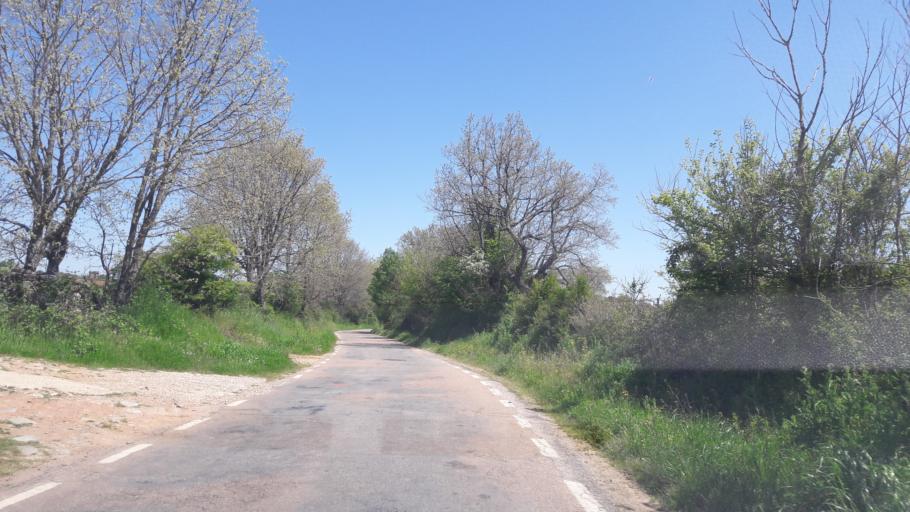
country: ES
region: Castille and Leon
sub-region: Provincia de Salamanca
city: Endrinal
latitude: 40.5851
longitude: -5.8056
